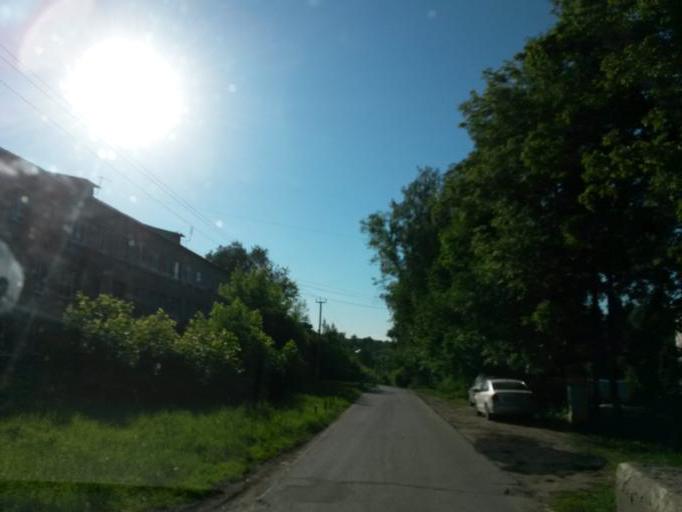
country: RU
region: Moskovskaya
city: Lyubuchany
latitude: 55.2423
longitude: 37.5430
